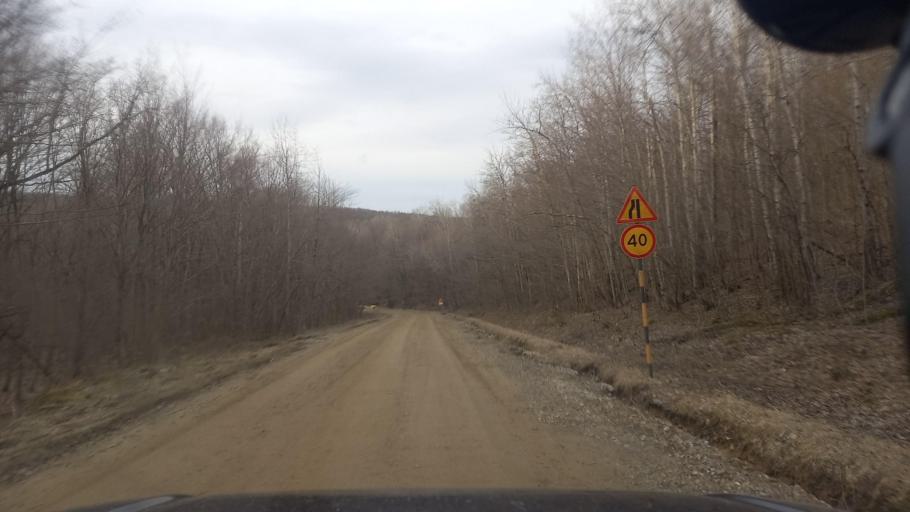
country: RU
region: Krasnodarskiy
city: Goryachiy Klyuch
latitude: 44.7035
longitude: 39.0162
